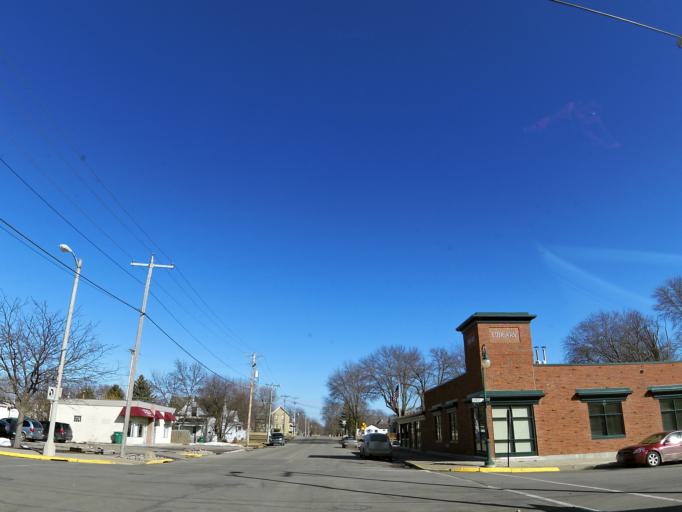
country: US
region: Minnesota
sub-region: Le Sueur County
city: Montgomery
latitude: 44.4356
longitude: -93.5813
